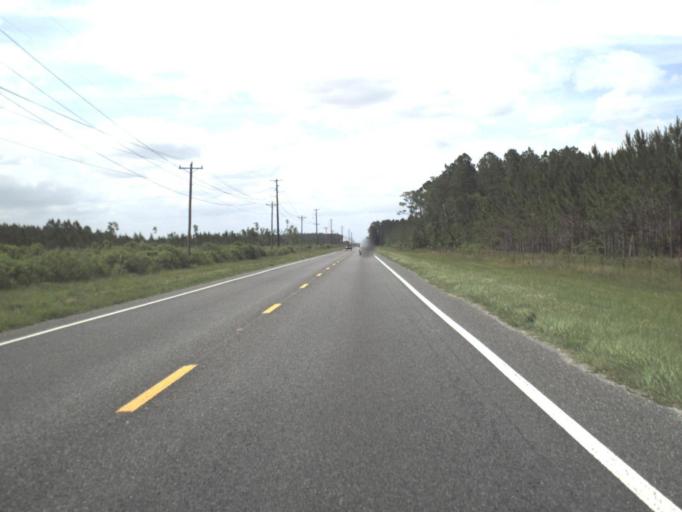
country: US
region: Florida
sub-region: Clay County
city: Middleburg
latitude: 29.9871
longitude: -81.8977
